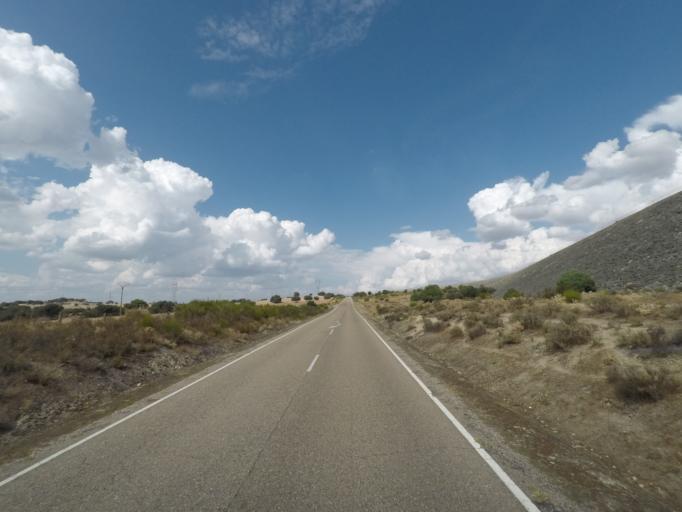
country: ES
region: Castille and Leon
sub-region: Provincia de Salamanca
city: Almendra
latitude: 41.2869
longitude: -6.3329
